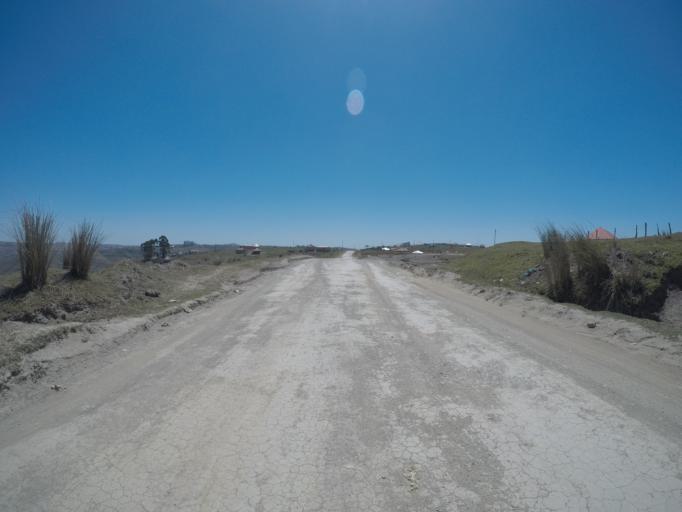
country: ZA
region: Eastern Cape
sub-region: OR Tambo District Municipality
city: Libode
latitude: -31.9435
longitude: 29.0274
